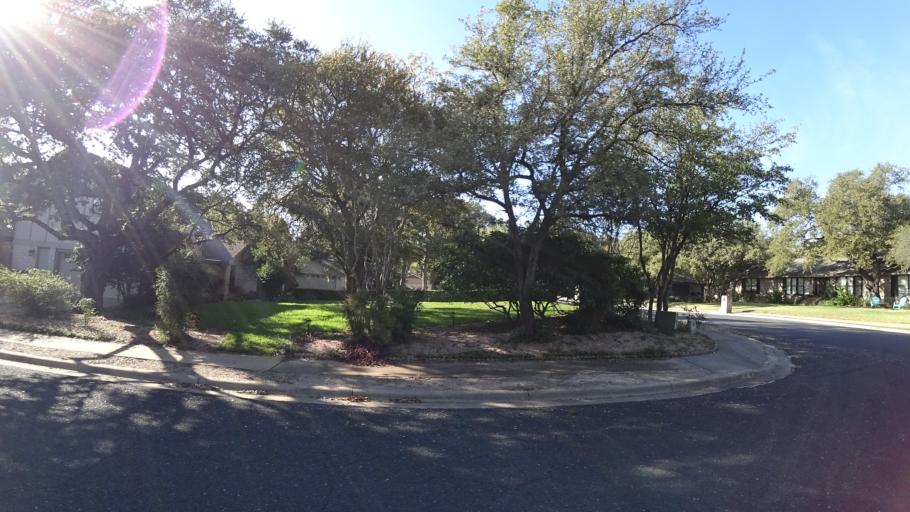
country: US
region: Texas
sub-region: Williamson County
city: Anderson Mill
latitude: 30.4421
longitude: -97.8105
